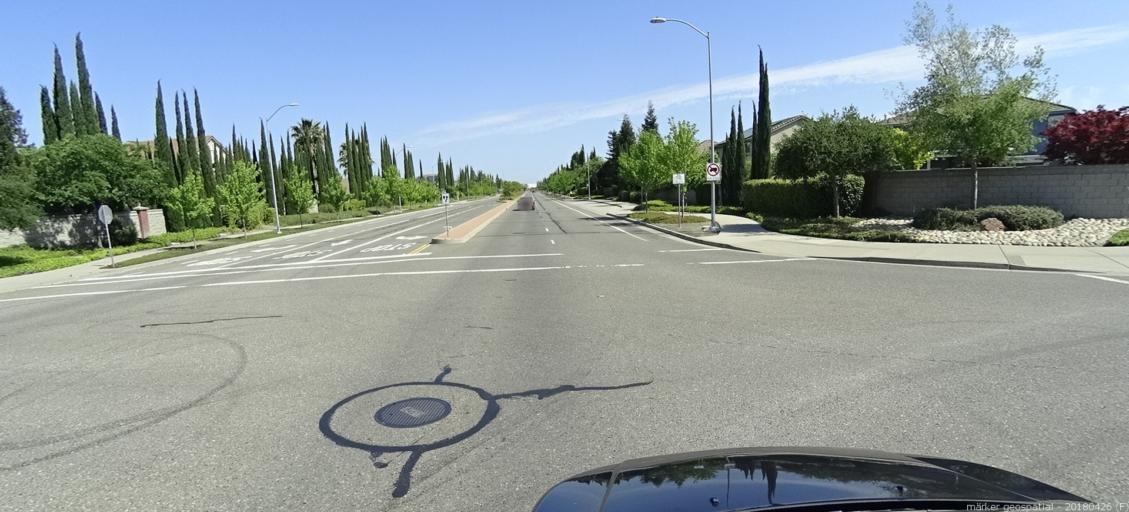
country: US
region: California
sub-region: Yolo County
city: West Sacramento
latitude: 38.5351
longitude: -121.5761
